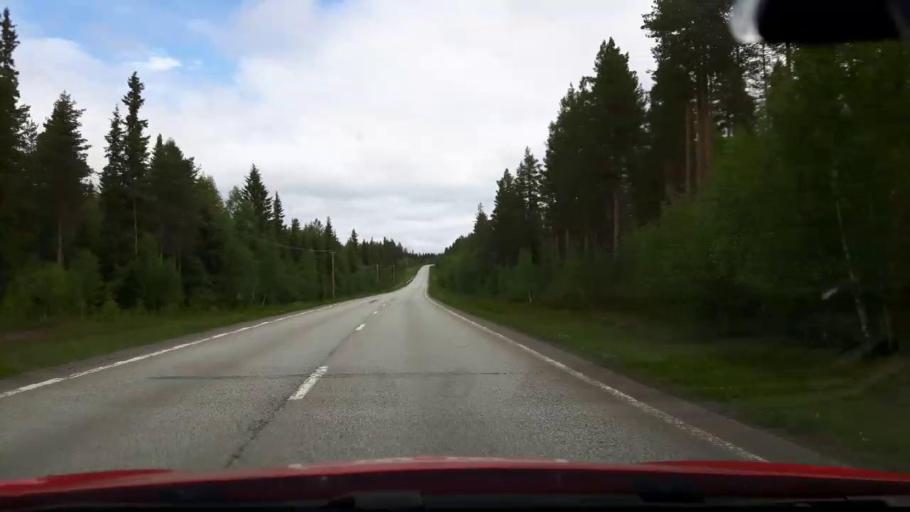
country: SE
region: Jaemtland
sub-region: Krokoms Kommun
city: Krokom
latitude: 63.4603
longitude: 14.4918
